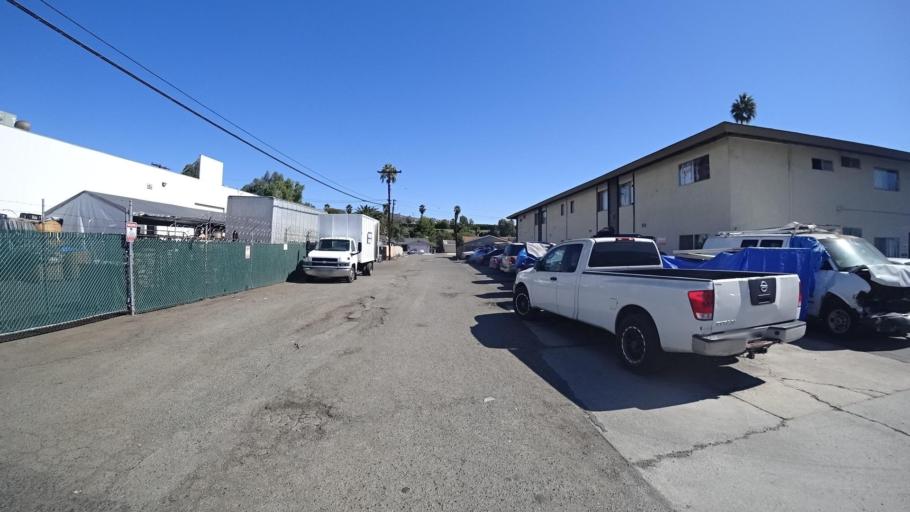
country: US
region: California
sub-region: San Diego County
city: La Presa
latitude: 32.7130
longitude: -117.0160
